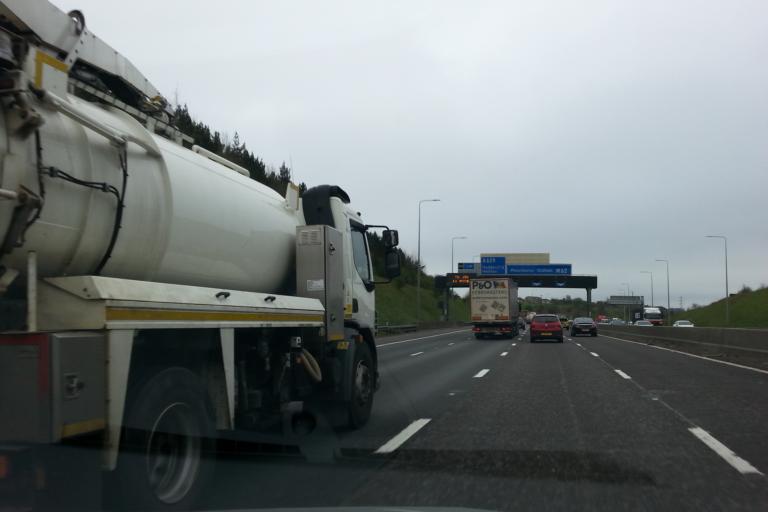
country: GB
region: England
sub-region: Calderdale
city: Elland
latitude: 53.6771
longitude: -1.8143
